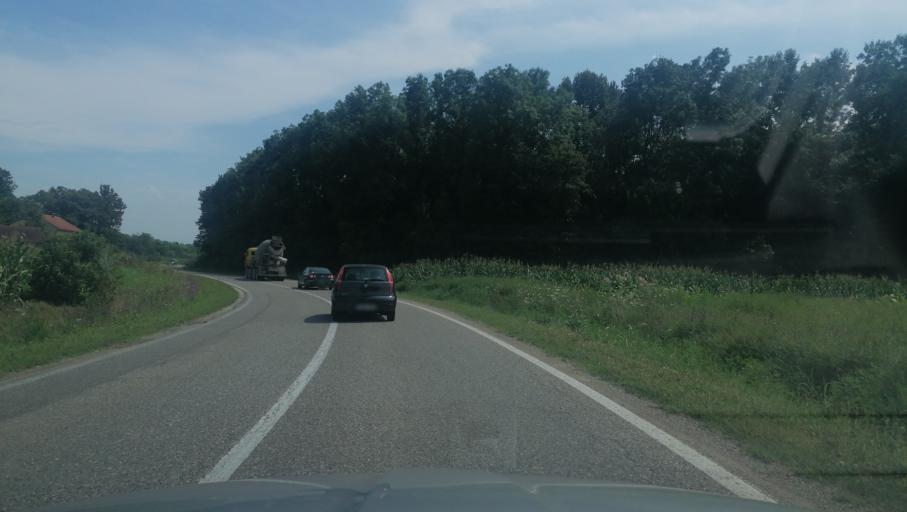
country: BA
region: Republika Srpska
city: Velika Obarska
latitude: 44.7888
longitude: 19.0870
